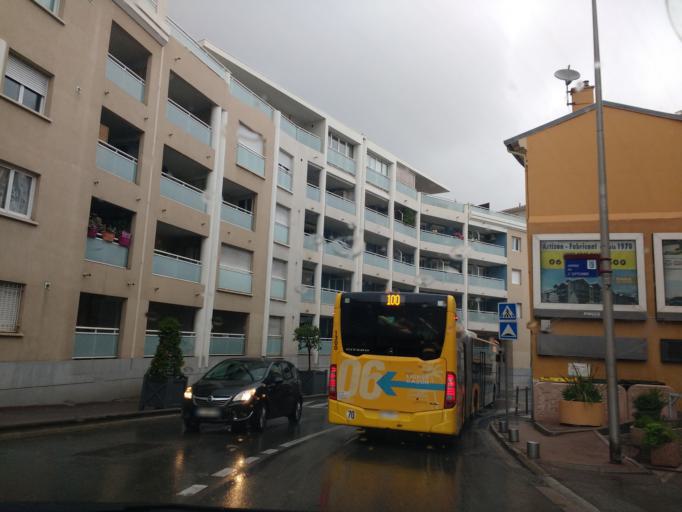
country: FR
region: Provence-Alpes-Cote d'Azur
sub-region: Departement des Alpes-Maritimes
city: Cap-d'Ail
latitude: 43.7255
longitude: 7.4097
